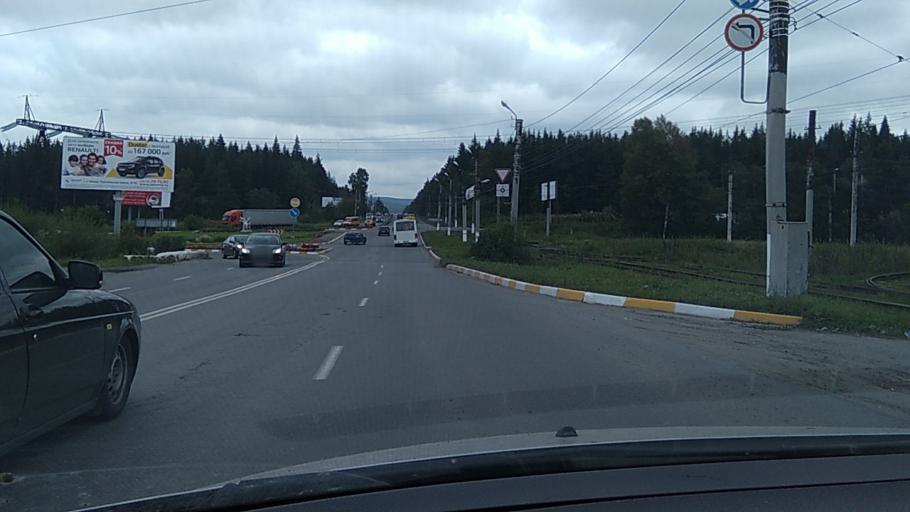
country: RU
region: Chelyabinsk
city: Zlatoust
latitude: 55.1372
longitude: 59.6709
